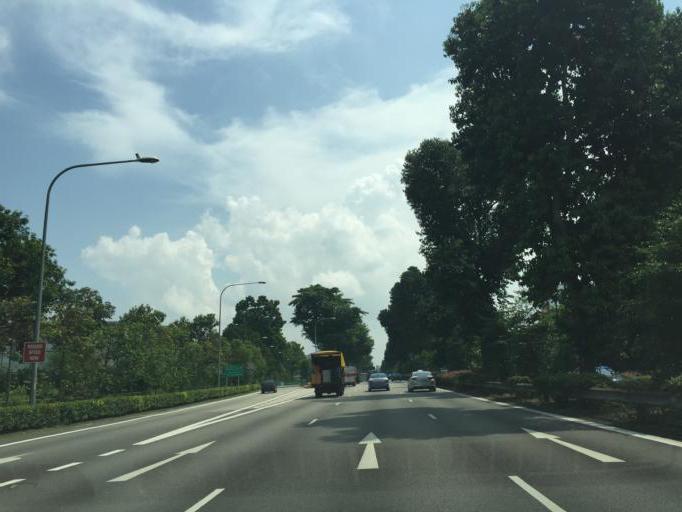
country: SG
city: Singapore
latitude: 1.3350
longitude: 103.9370
